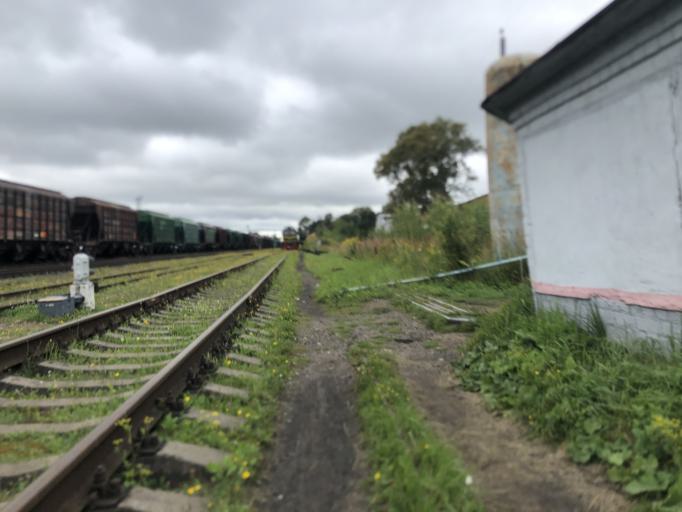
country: RU
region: Tverskaya
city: Rzhev
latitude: 56.2395
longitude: 34.3334
